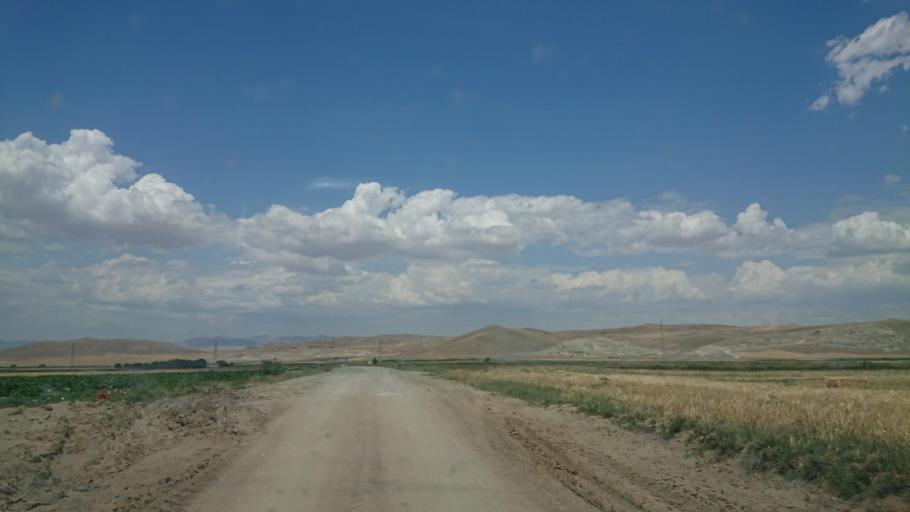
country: TR
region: Aksaray
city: Sariyahsi
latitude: 38.9767
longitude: 33.9011
